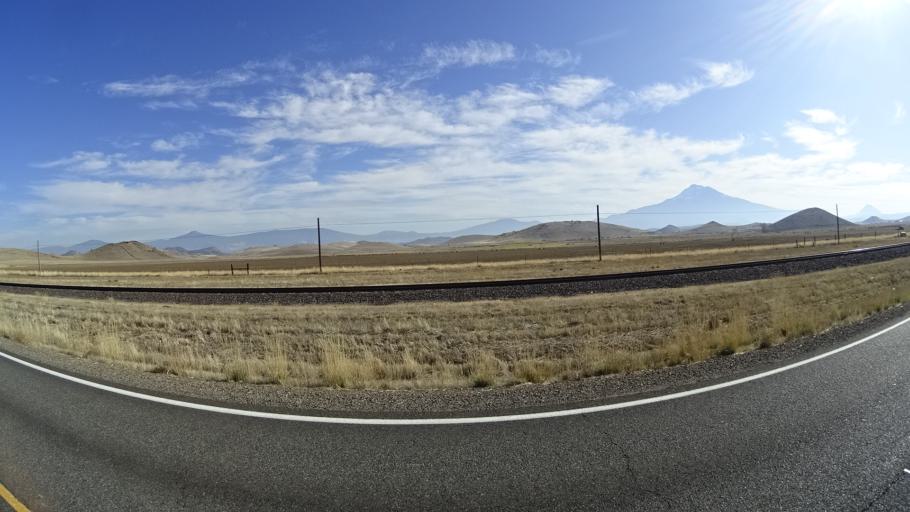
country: US
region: California
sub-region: Siskiyou County
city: Montague
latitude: 41.5476
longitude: -122.5261
